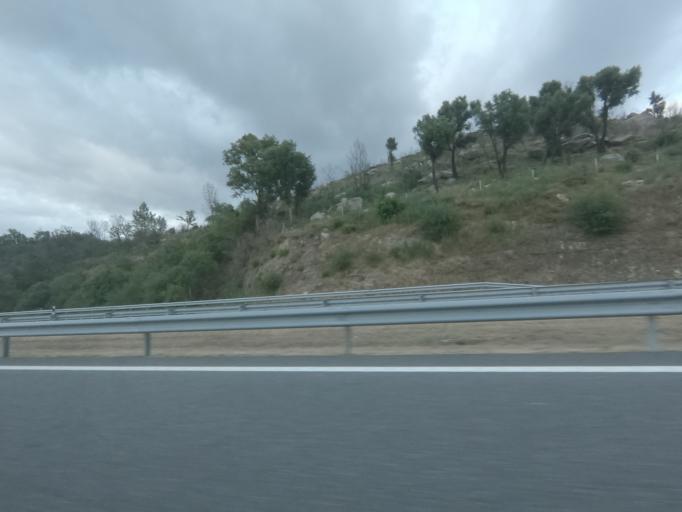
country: ES
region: Galicia
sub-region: Provincia de Ourense
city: Carballeda de Avia
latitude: 42.3036
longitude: -8.1786
